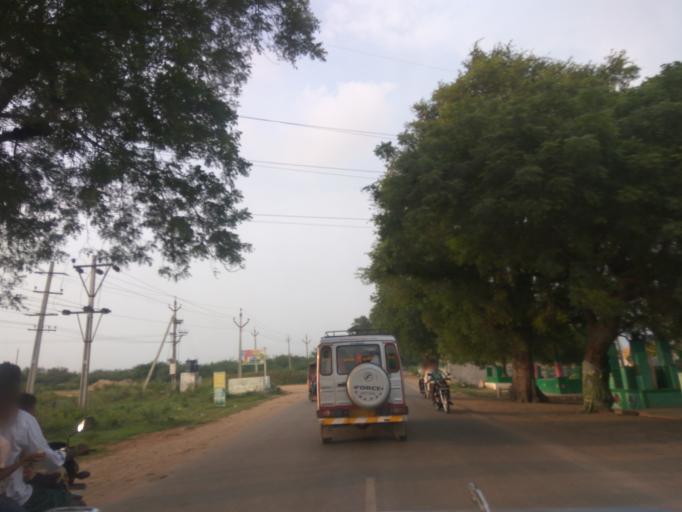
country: IN
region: Andhra Pradesh
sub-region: Guntur
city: Vinukonda
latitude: 16.0663
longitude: 79.7417
